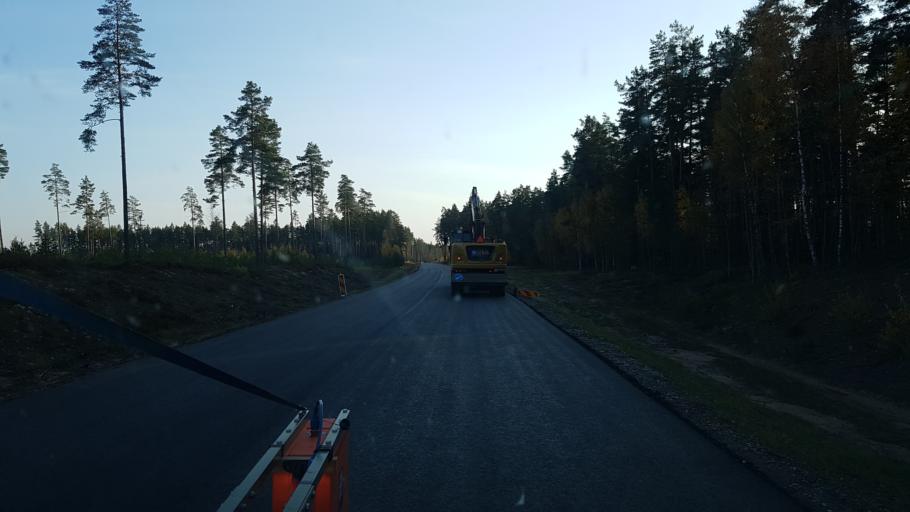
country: EE
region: Polvamaa
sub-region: Polva linn
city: Polva
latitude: 57.9274
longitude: 27.1826
